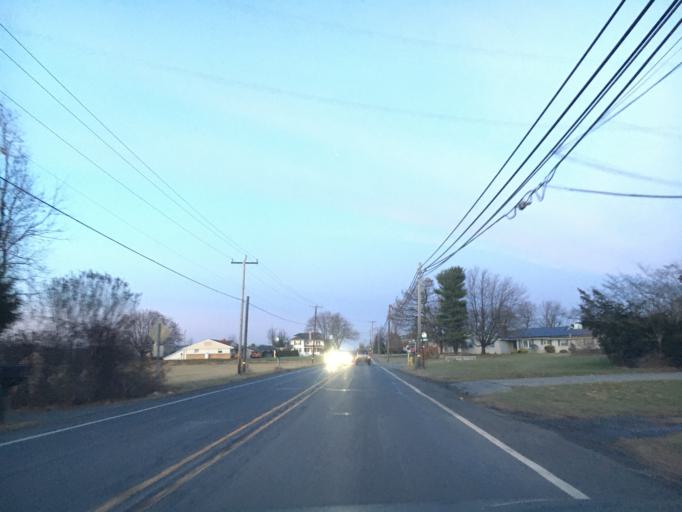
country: US
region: Pennsylvania
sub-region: Lehigh County
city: Schnecksville
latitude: 40.6855
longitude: -75.6125
